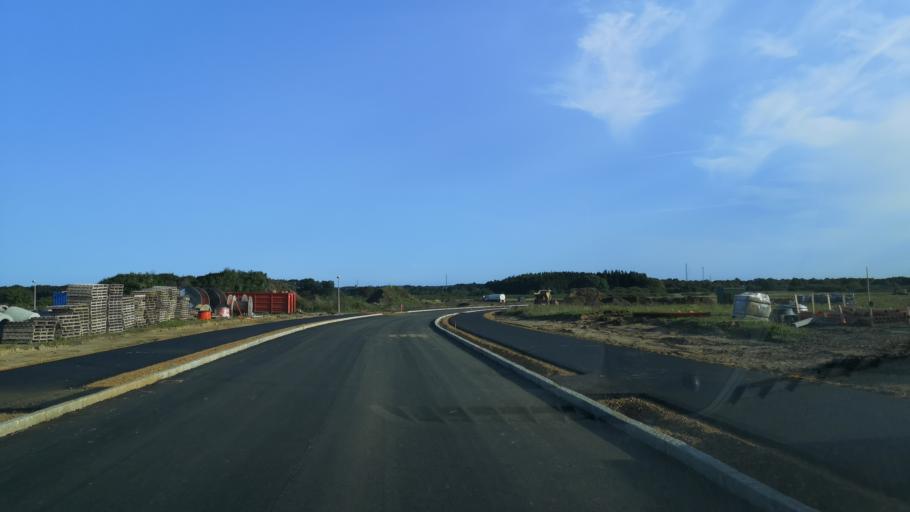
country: DK
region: Central Jutland
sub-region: Herning Kommune
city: Snejbjerg
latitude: 56.1388
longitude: 8.9191
